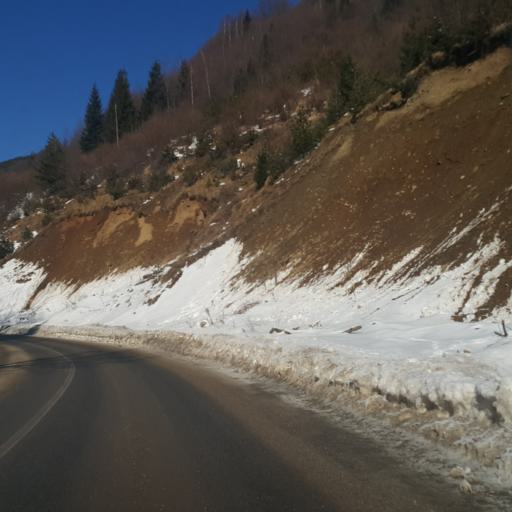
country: XK
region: Mitrovica
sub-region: Komuna e Leposaviqit
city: Leposaviq
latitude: 43.3041
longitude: 20.8794
